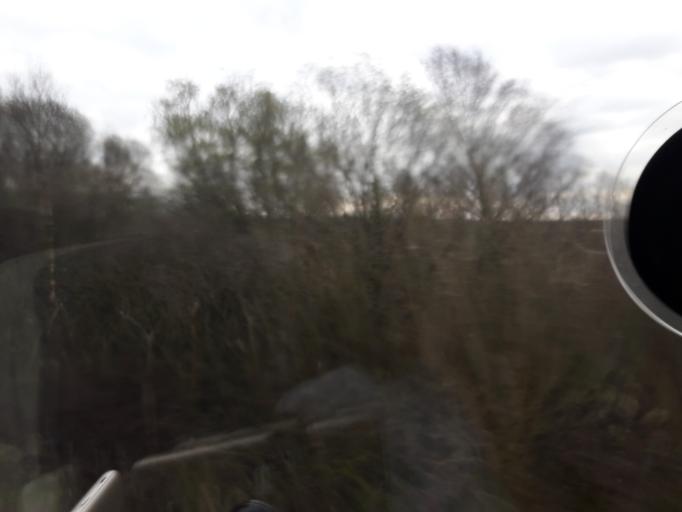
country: IE
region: Leinster
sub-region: An Longfort
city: Granard
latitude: 53.6630
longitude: -7.4617
